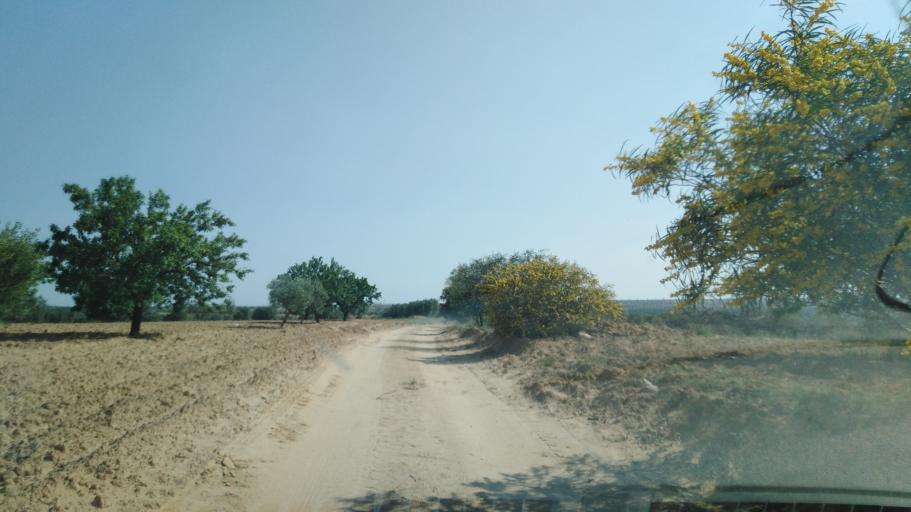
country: TN
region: Safaqis
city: Bi'r `Ali Bin Khalifah
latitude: 34.7854
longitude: 10.3697
